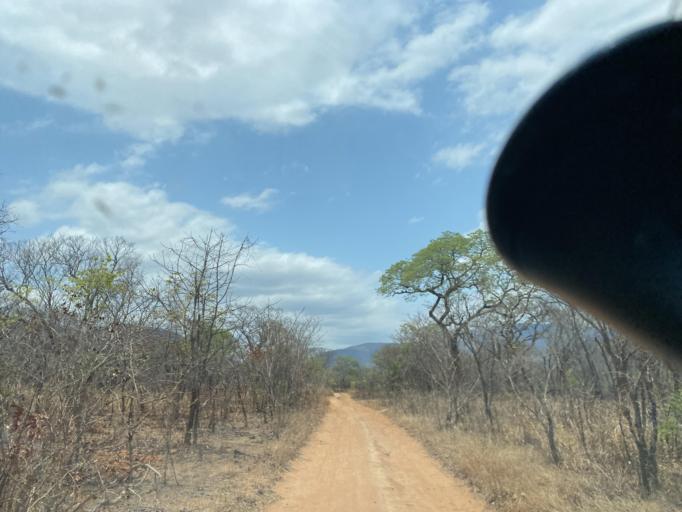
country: ZM
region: Lusaka
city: Luangwa
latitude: -15.1796
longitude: 29.7164
